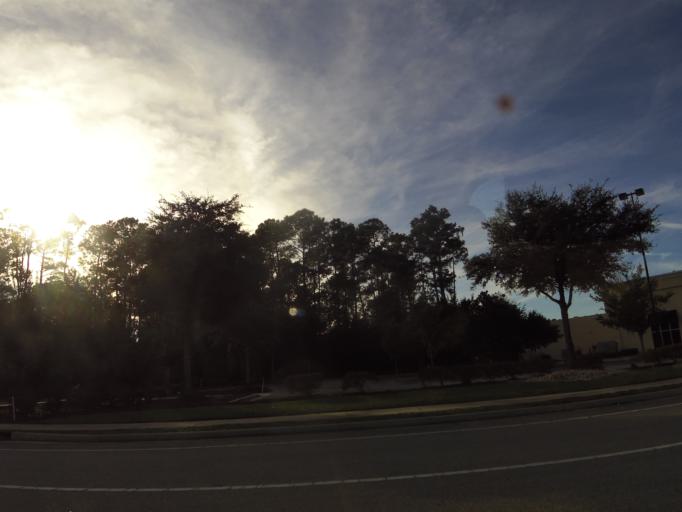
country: US
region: Florida
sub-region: Saint Johns County
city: Fruit Cove
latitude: 30.1759
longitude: -81.5564
